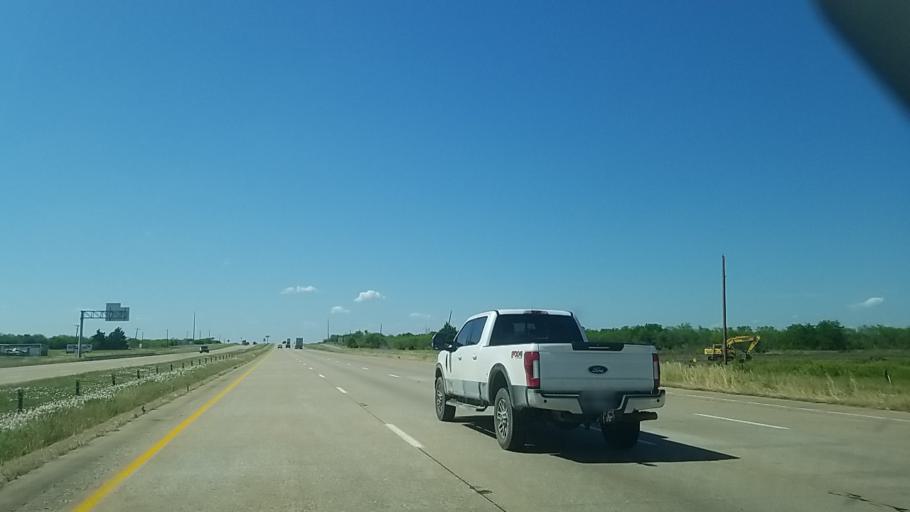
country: US
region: Texas
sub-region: Ellis County
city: Ennis
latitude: 32.3793
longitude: -96.6475
